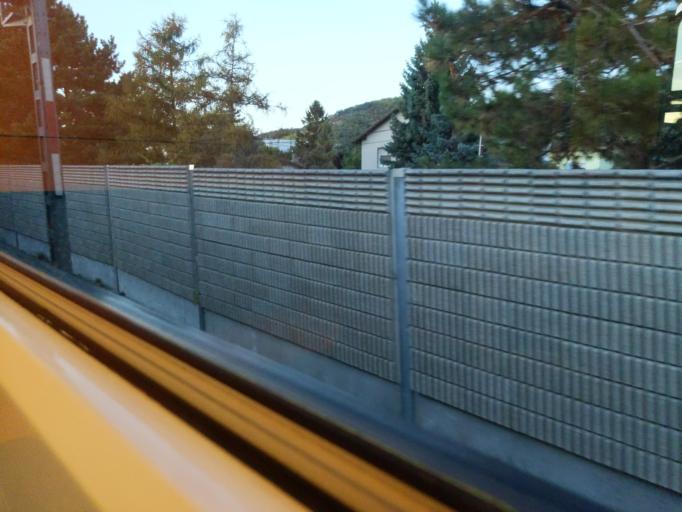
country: AT
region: Lower Austria
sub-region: Politischer Bezirk Korneuburg
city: Langenzersdorf
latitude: 48.3043
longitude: 16.3590
